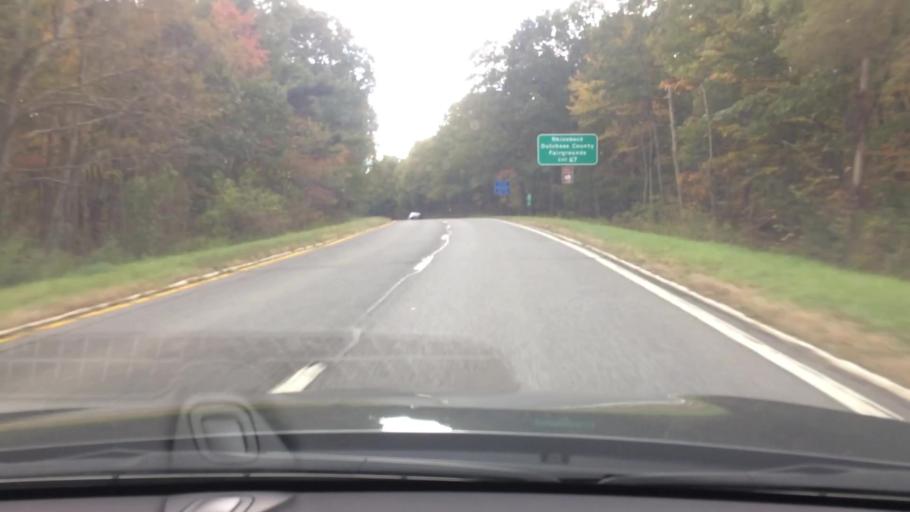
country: US
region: New York
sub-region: Dutchess County
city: Pine Plains
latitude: 41.9714
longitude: -73.7523
